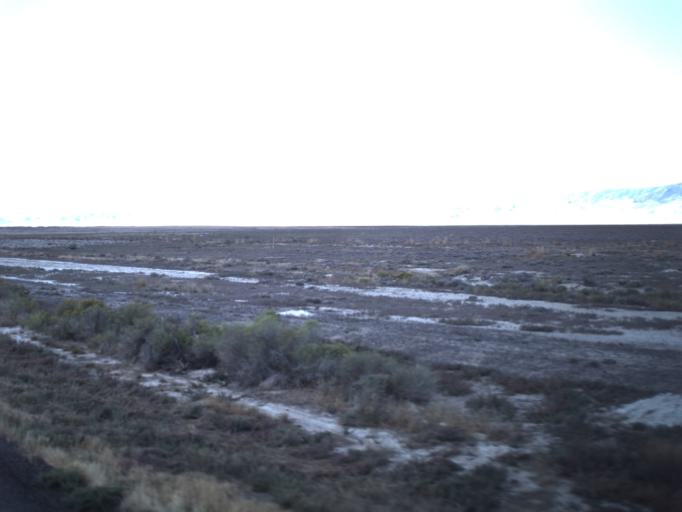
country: US
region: Utah
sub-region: Millard County
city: Delta
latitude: 38.9969
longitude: -112.7888
